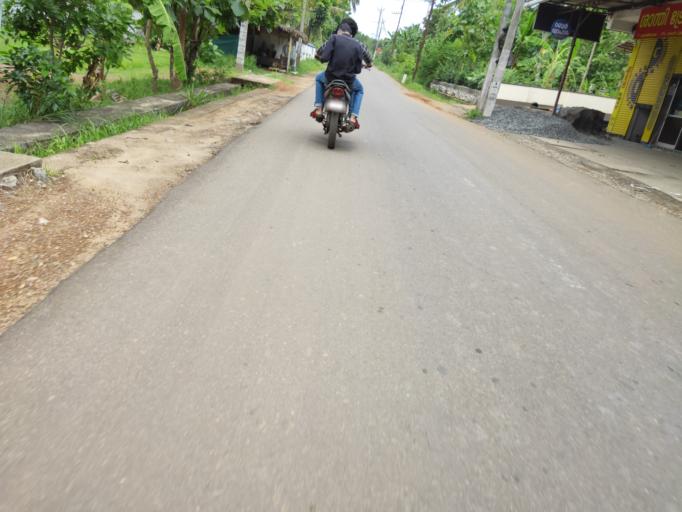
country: IN
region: Kerala
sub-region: Malappuram
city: Manjeri
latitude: 11.2087
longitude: 76.2597
